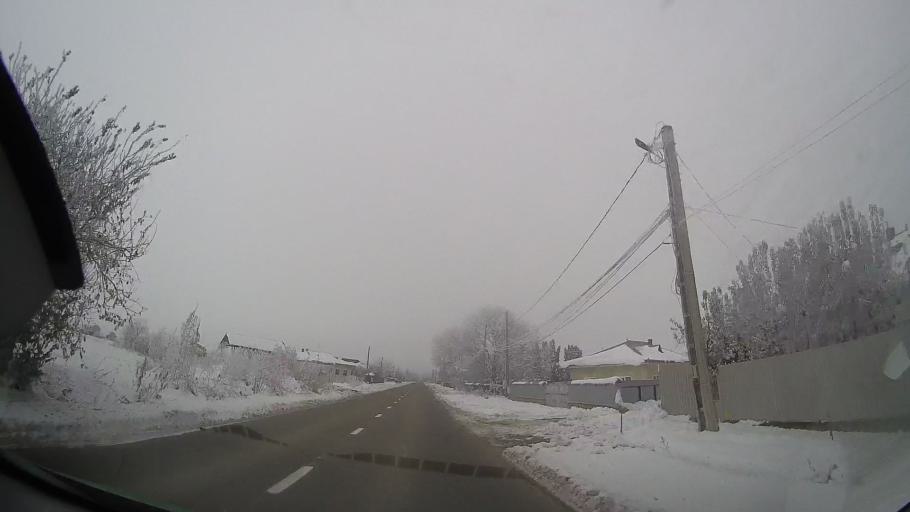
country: RO
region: Neamt
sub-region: Comuna Horia
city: Cotu Vames
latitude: 46.8961
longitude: 26.9598
